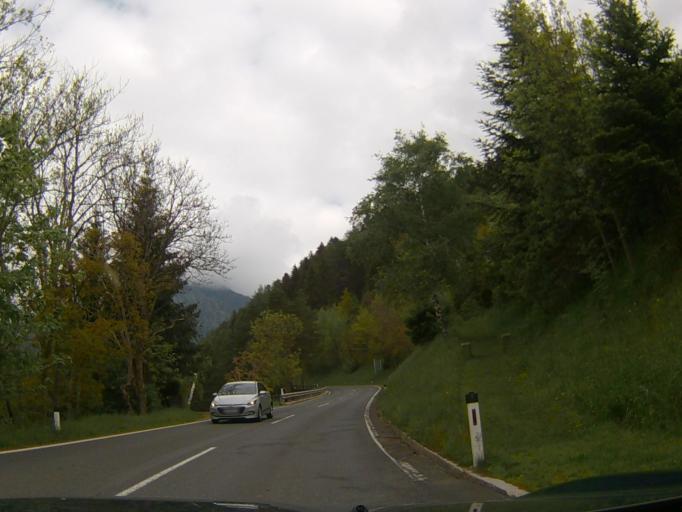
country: AT
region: Carinthia
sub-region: Politischer Bezirk Spittal an der Drau
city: Obervellach
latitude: 46.9364
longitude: 13.1982
